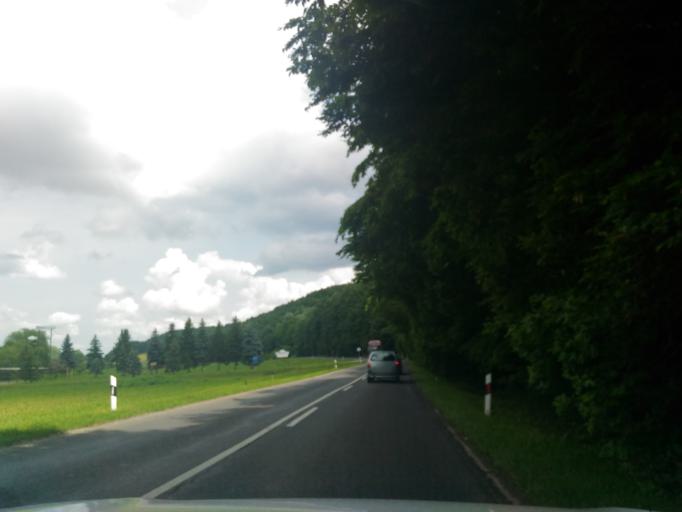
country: HU
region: Baranya
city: Komlo
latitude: 46.1641
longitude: 18.2152
